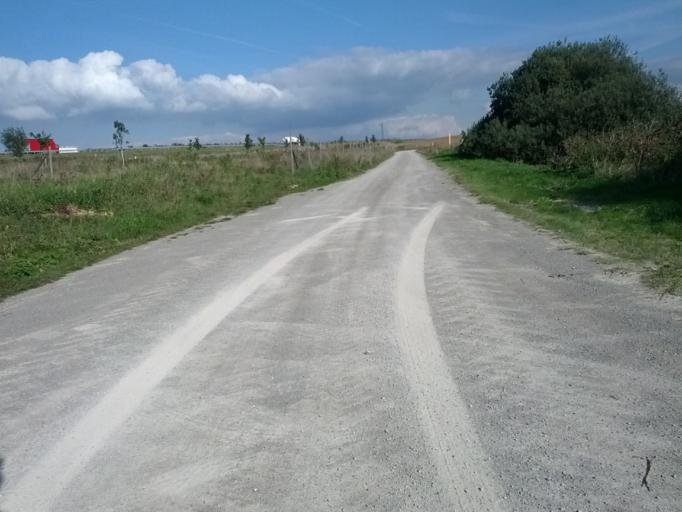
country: DE
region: Thuringia
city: Eisenach
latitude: 51.0139
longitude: 10.3247
